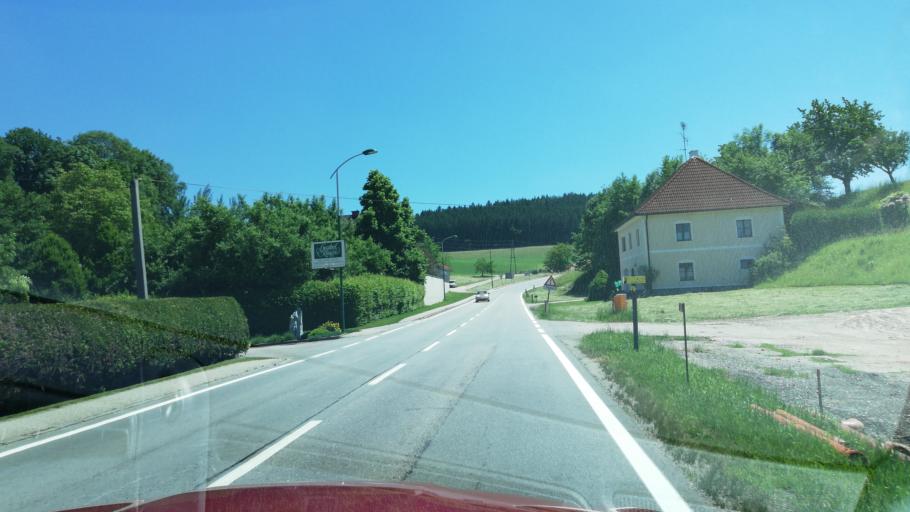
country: AT
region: Upper Austria
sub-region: Politischer Bezirk Vocklabruck
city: Niederthalheim
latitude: 48.1380
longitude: 13.7341
